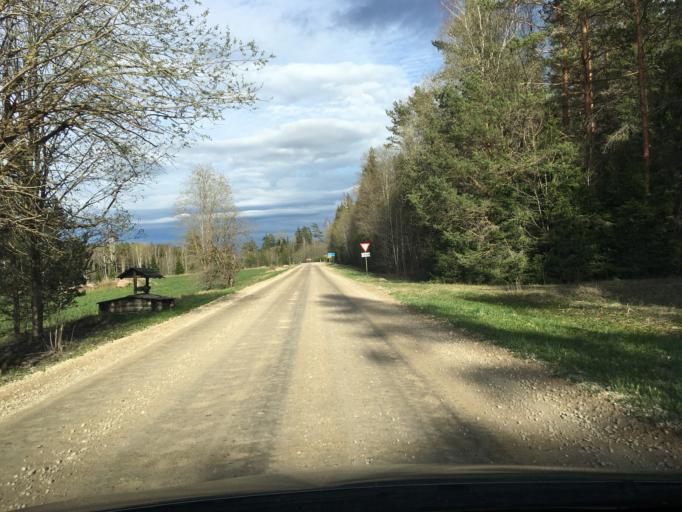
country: EE
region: Raplamaa
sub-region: Maerjamaa vald
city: Marjamaa
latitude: 59.0236
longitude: 24.4449
